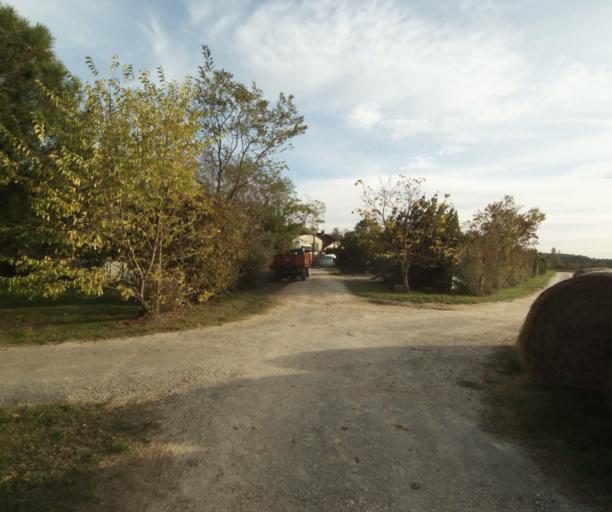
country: FR
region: Midi-Pyrenees
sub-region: Departement du Tarn-et-Garonne
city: Campsas
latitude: 43.8820
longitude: 1.3432
